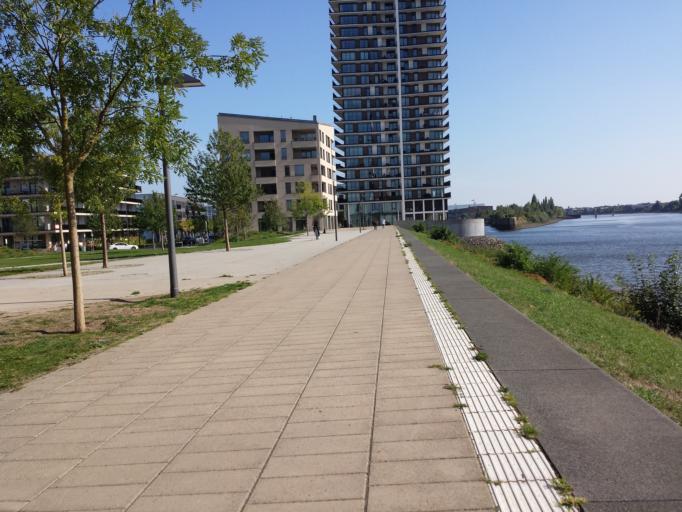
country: DE
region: Bremen
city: Bremen
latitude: 53.0987
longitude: 8.7583
